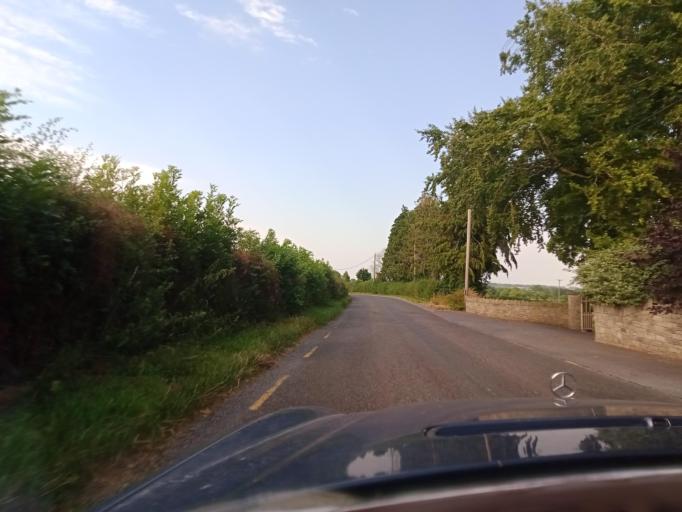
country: IE
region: Leinster
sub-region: Kilkenny
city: Callan
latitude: 52.5217
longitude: -7.3014
